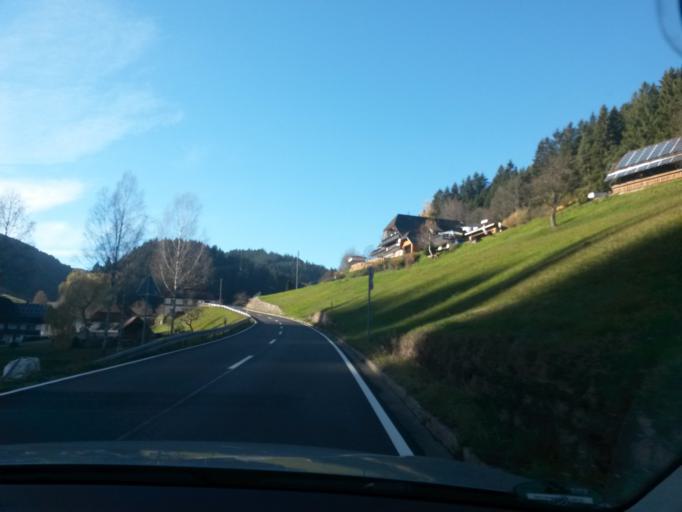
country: DE
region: Baden-Wuerttemberg
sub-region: Karlsruhe Region
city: Bad Rippoldsau-Schapbach
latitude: 48.4478
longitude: 8.2998
